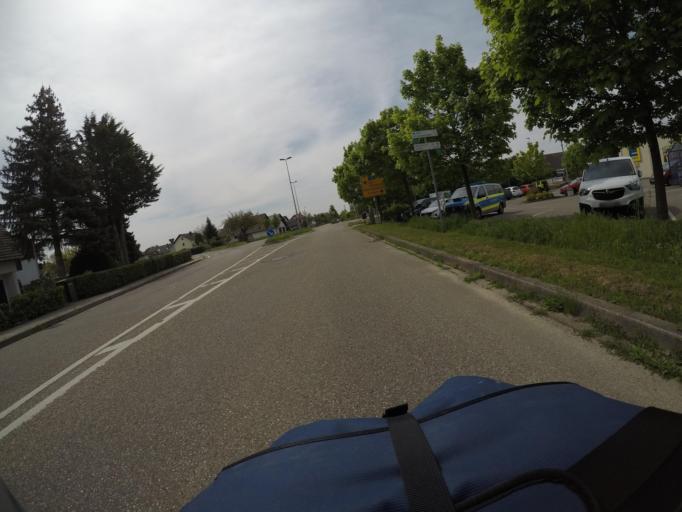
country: DE
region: Baden-Wuerttemberg
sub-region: Karlsruhe Region
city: Schwarzach
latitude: 48.7486
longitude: 8.0387
